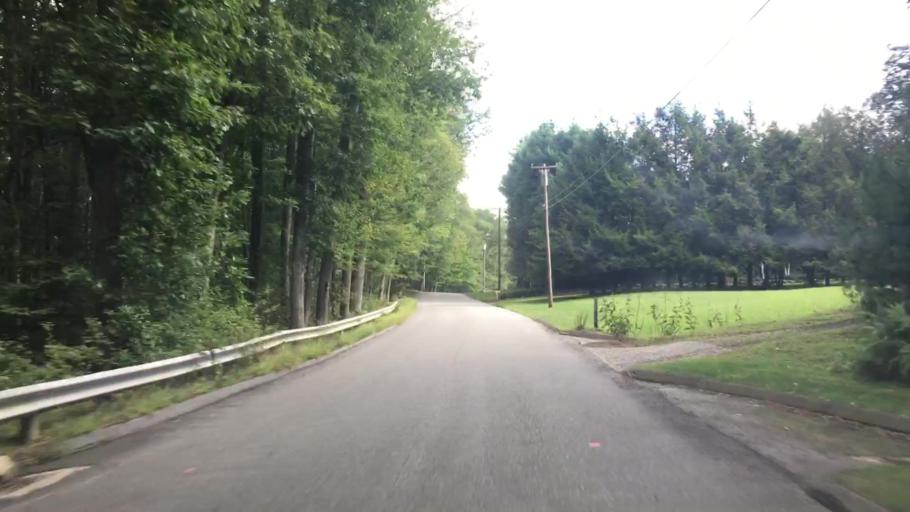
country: US
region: Connecticut
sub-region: Tolland County
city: Stafford Springs
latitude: 41.9180
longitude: -72.2198
